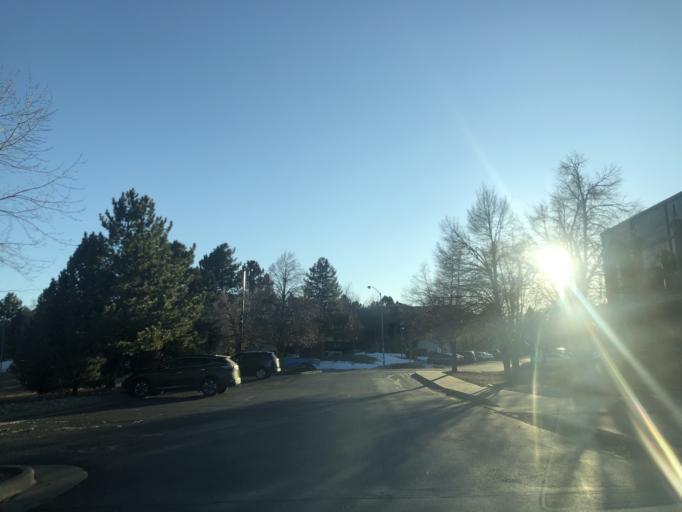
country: US
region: Colorado
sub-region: Adams County
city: Aurora
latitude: 39.7198
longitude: -104.8142
